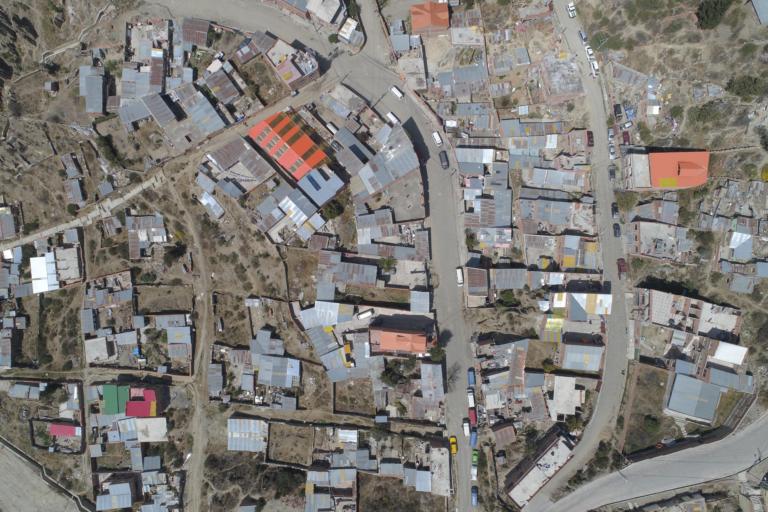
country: BO
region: La Paz
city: La Paz
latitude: -16.4982
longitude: -68.0979
